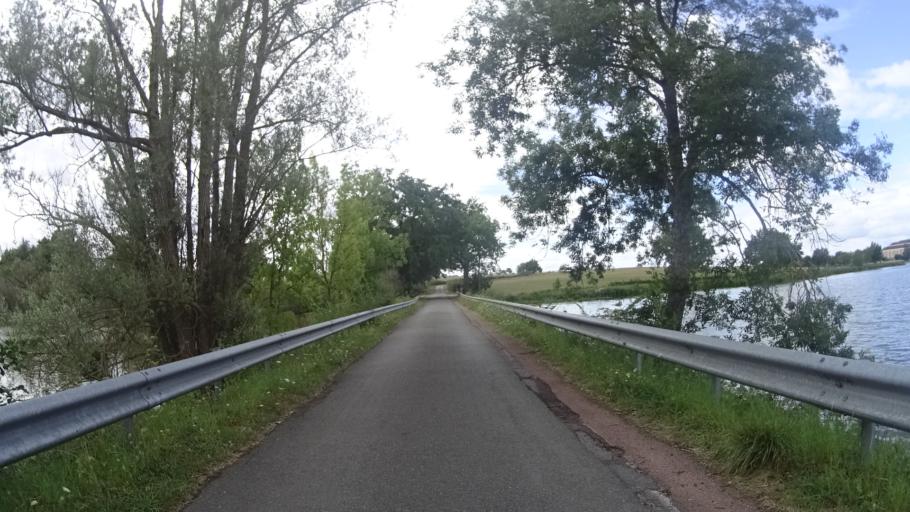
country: FR
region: Bourgogne
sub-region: Departement de Saone-et-Loire
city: Saint-Leu
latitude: 46.7438
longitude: 4.4953
